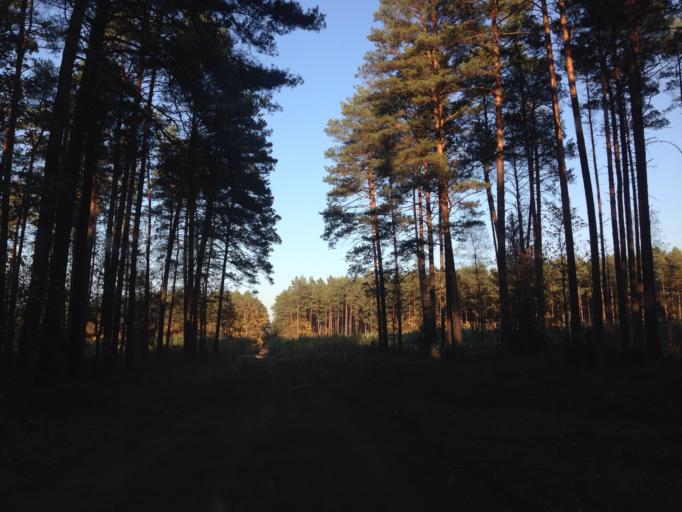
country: PL
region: Kujawsko-Pomorskie
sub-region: Powiat brodnicki
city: Gorzno
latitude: 53.1655
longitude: 19.7354
